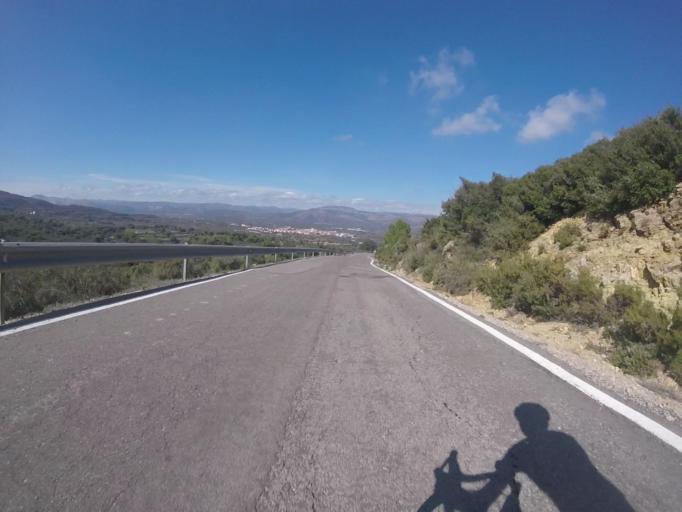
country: ES
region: Valencia
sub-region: Provincia de Castello
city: Albocasser
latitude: 40.3507
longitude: 0.0478
